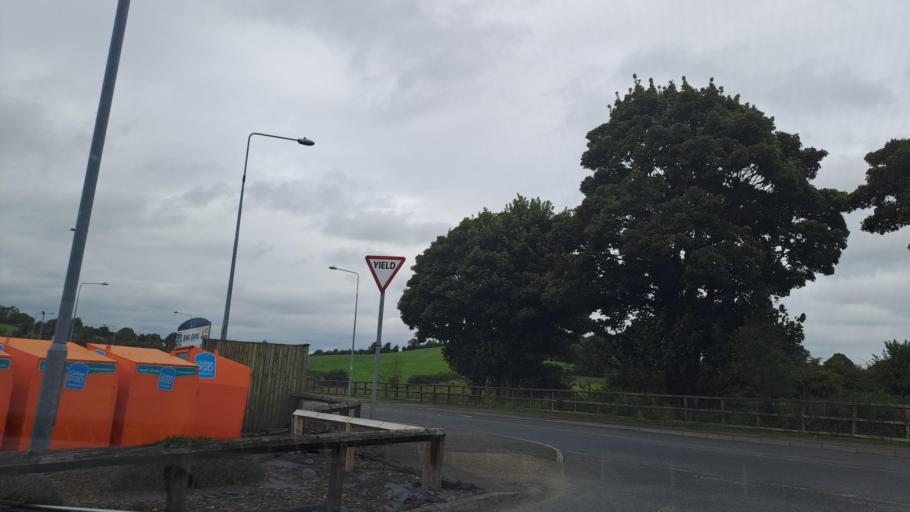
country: IE
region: Ulster
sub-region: An Cabhan
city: Bailieborough
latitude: 53.9177
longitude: -6.9671
